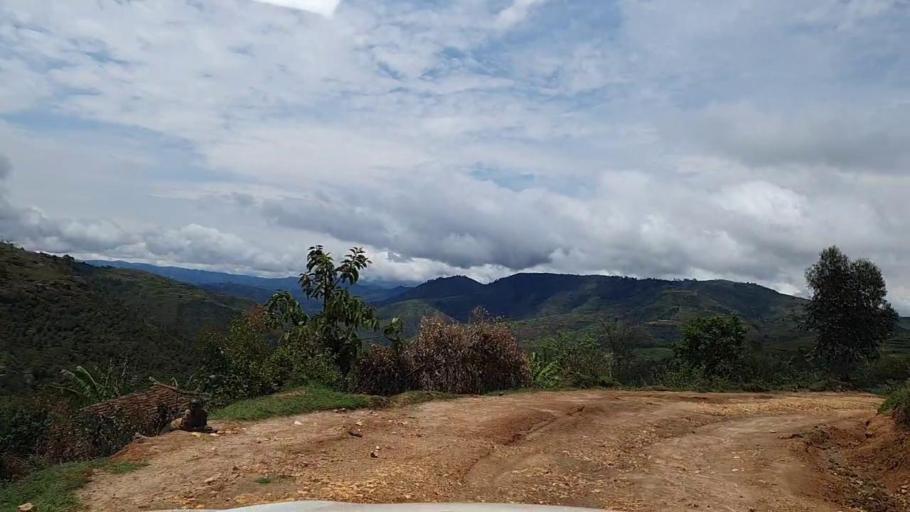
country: RW
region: Southern Province
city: Gikongoro
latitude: -2.3410
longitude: 29.5124
